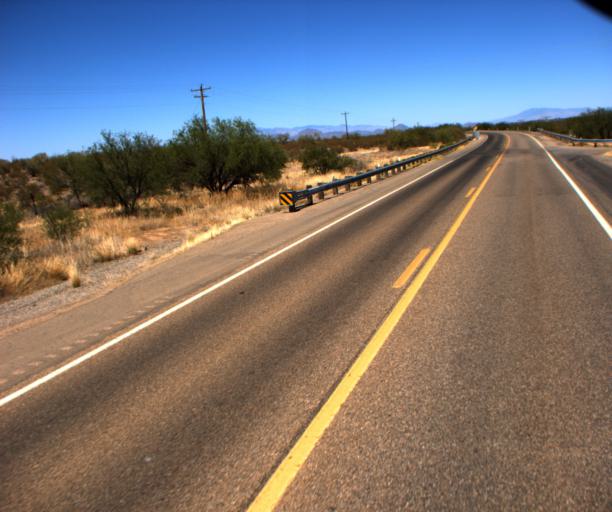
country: US
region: Arizona
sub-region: Pima County
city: Three Points
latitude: 32.0660
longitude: -111.3689
